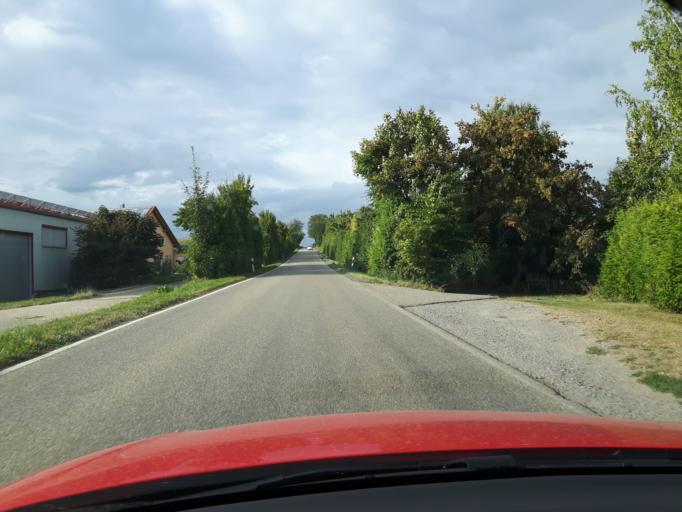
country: DE
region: Baden-Wuerttemberg
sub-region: Regierungsbezirk Stuttgart
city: Nordheim
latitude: 49.0819
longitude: 9.1059
